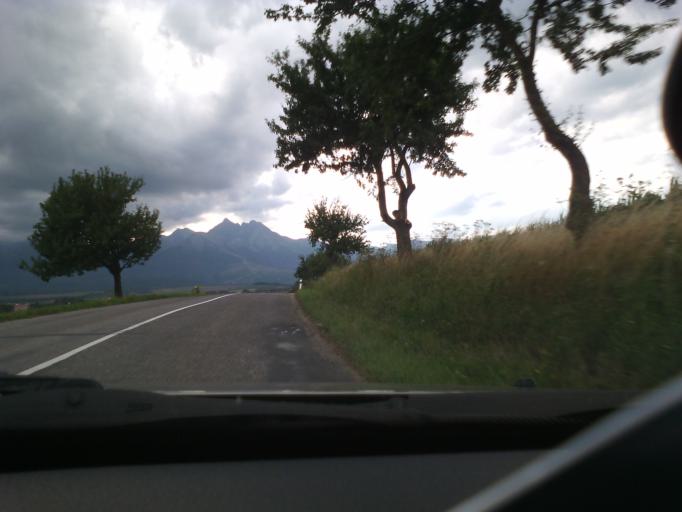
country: SK
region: Presovsky
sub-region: Okres Presov
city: Kezmarok
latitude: 49.1081
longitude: 20.3809
